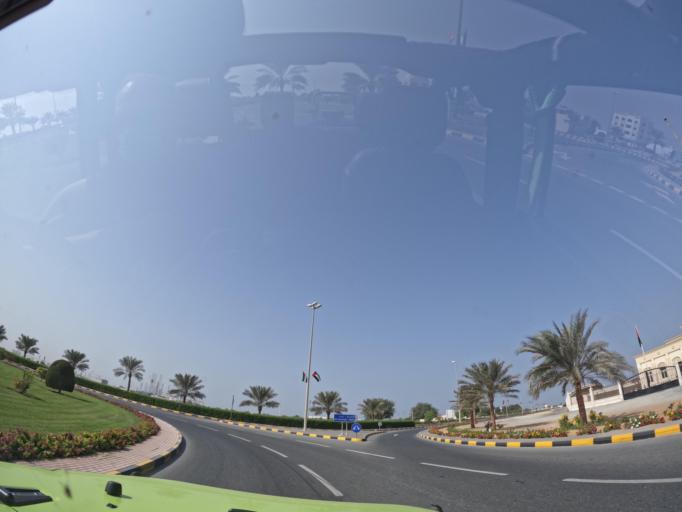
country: AE
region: Umm al Qaywayn
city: Umm al Qaywayn
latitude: 25.4796
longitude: 55.5222
